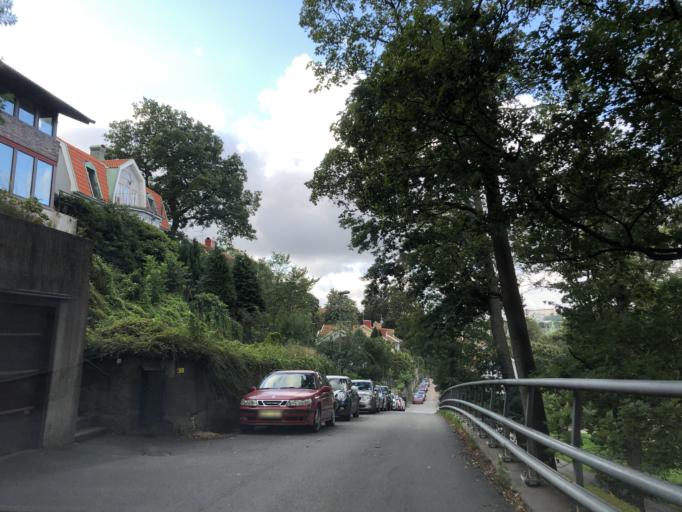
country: SE
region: Vaestra Goetaland
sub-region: Goteborg
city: Goeteborg
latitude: 57.7018
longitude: 11.9972
